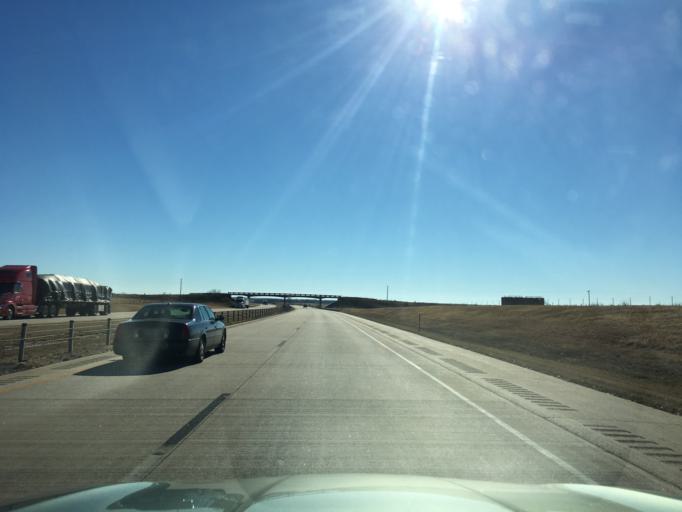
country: US
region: Oklahoma
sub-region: Kay County
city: Tonkawa
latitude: 36.5095
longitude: -97.3370
